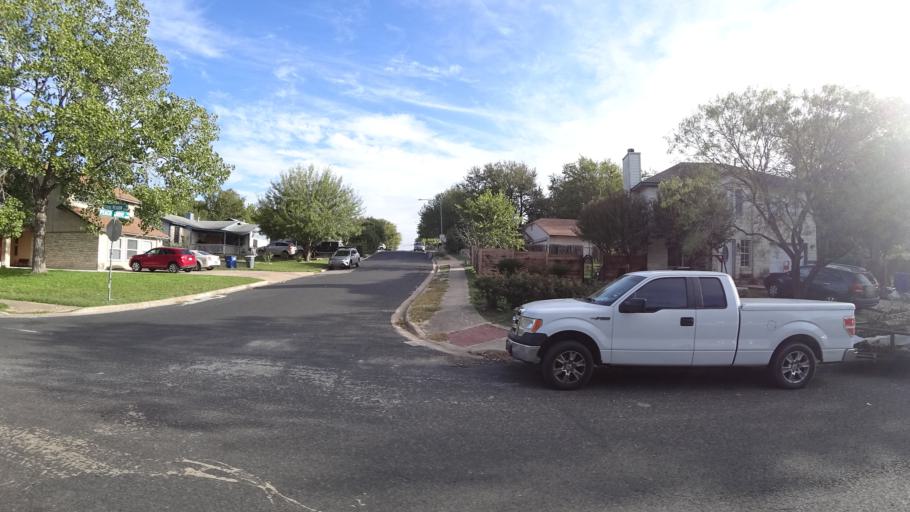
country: US
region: Texas
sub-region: Travis County
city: Austin
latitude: 30.1947
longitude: -97.7311
